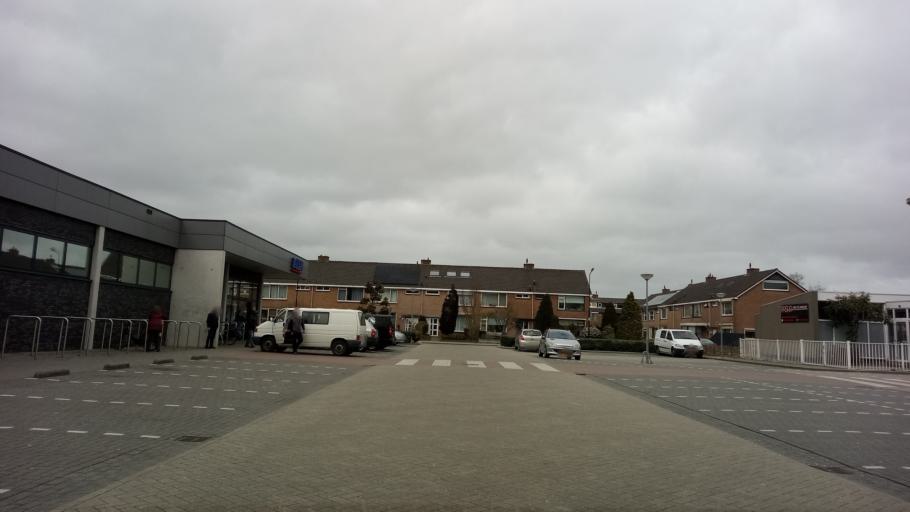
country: NL
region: North Holland
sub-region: Gemeente Heerhugowaard
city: Heerhugowaard
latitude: 52.6746
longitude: 4.8532
